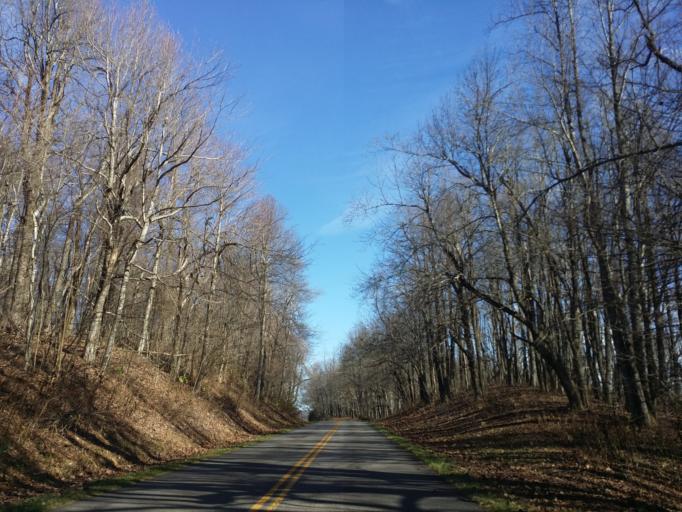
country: US
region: North Carolina
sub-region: Mitchell County
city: Spruce Pine
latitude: 35.7884
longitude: -82.1672
